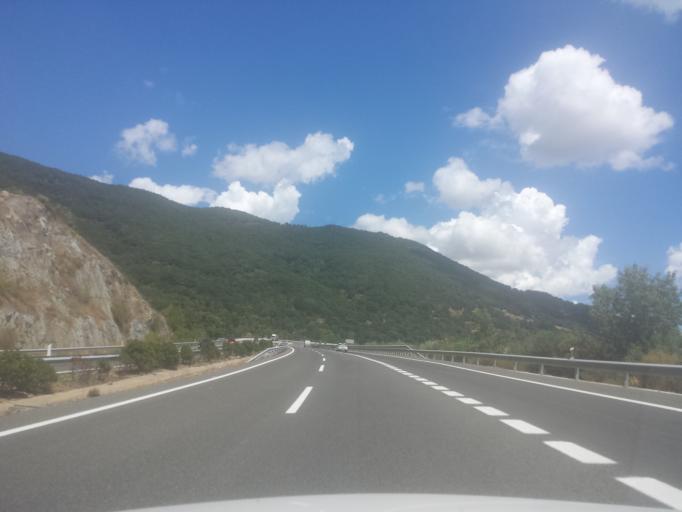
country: ES
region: Extremadura
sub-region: Provincia de Caceres
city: Banos de Montemayor
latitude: 40.3084
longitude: -5.8802
